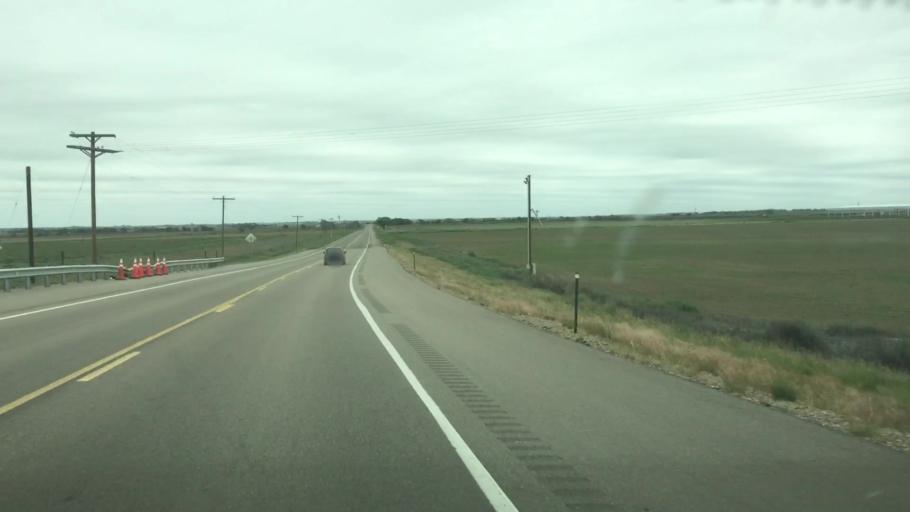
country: US
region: Colorado
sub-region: Prowers County
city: Lamar
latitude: 38.0529
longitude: -102.2524
